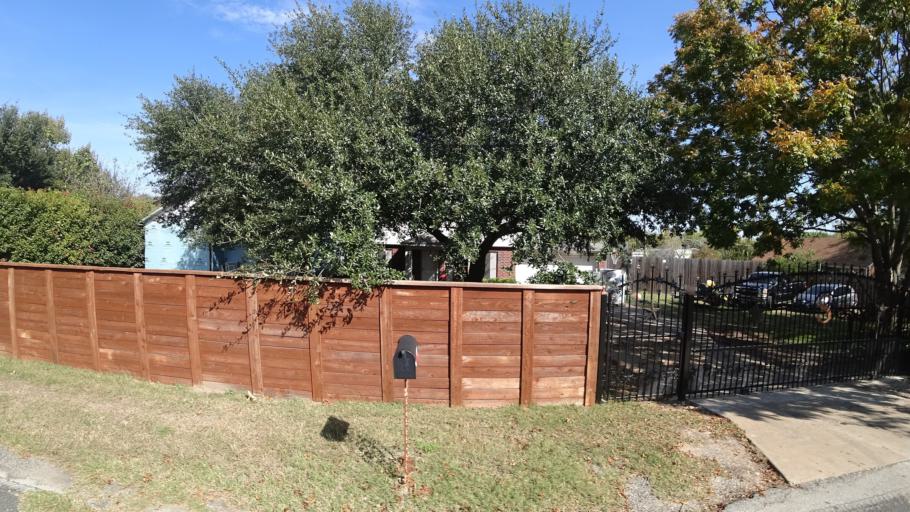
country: US
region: Texas
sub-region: Travis County
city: Pflugerville
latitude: 30.4143
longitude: -97.6286
